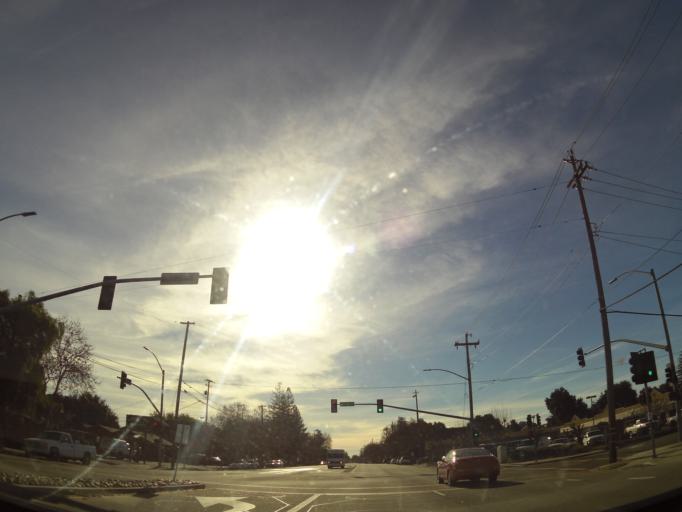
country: US
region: California
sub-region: Santa Clara County
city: Morgan Hill
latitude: 37.1351
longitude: -121.6587
